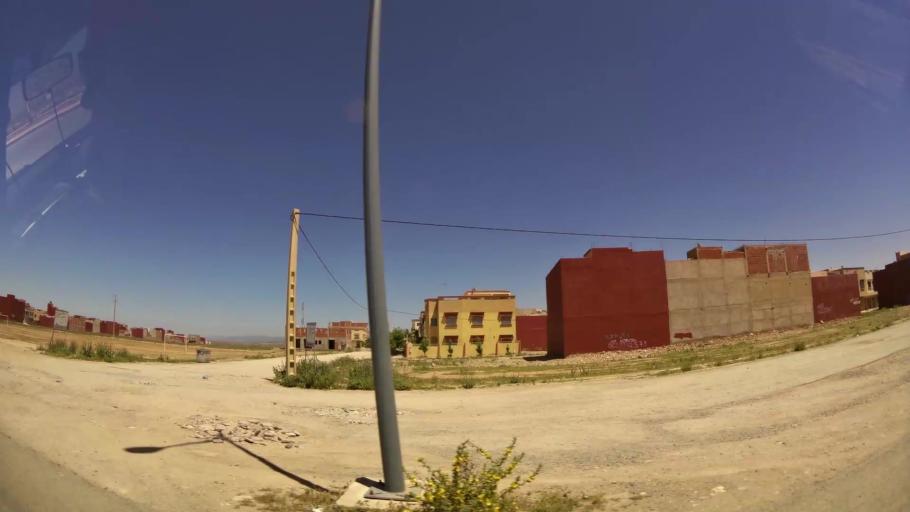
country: MA
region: Oriental
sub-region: Oujda-Angad
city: Oujda
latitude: 34.6780
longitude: -1.8595
